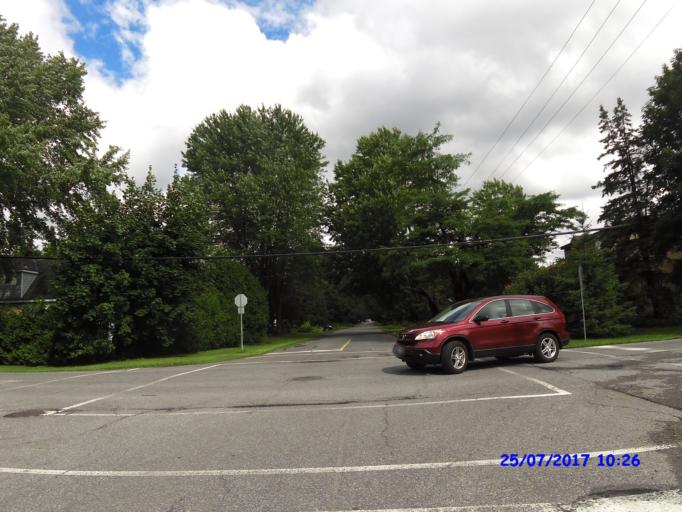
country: CA
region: Ontario
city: Ottawa
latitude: 45.3600
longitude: -75.7038
